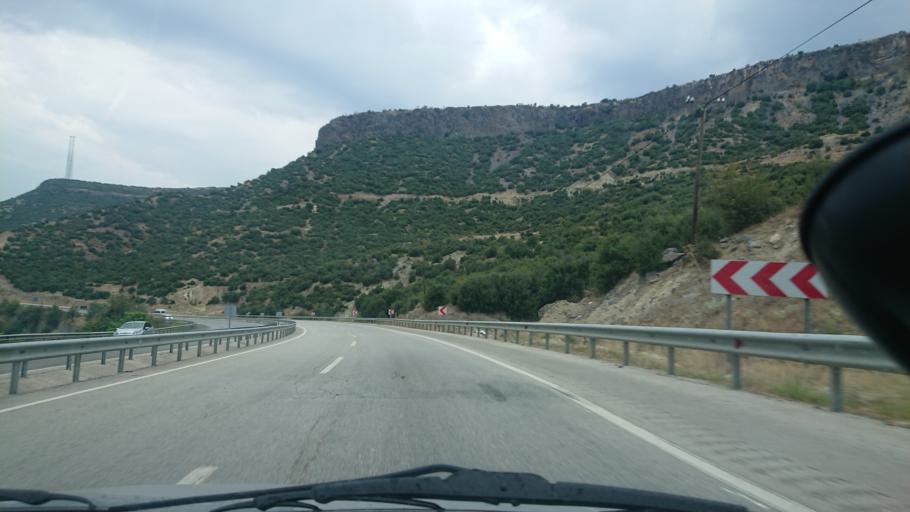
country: TR
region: Manisa
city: Selendi
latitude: 38.6157
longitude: 28.8287
